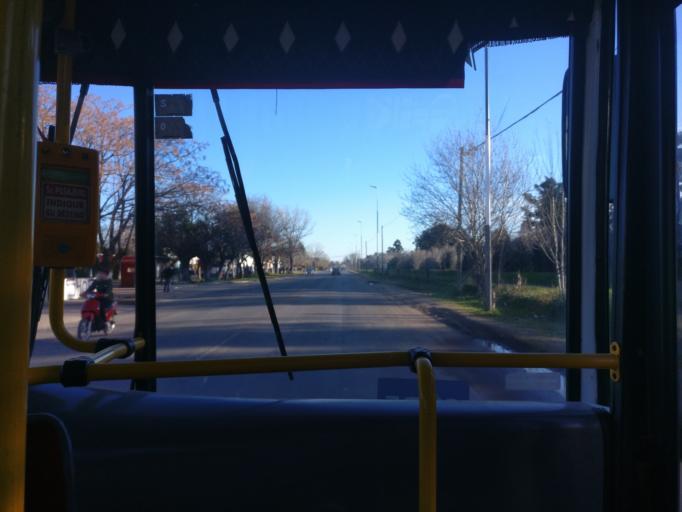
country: AR
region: Buenos Aires
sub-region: Partido de Ezeiza
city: Ezeiza
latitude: -34.9115
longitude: -58.5958
